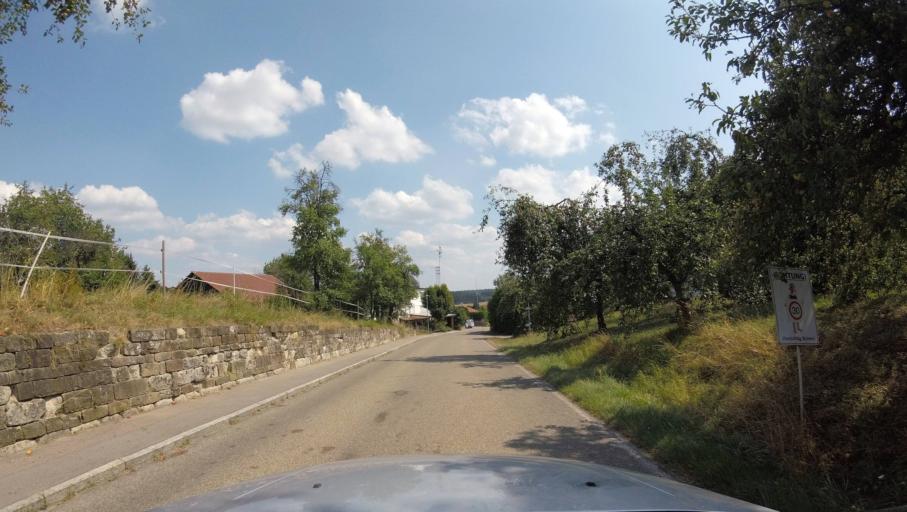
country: DE
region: Baden-Wuerttemberg
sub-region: Regierungsbezirk Stuttgart
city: Althutte
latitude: 48.9485
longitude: 9.5694
